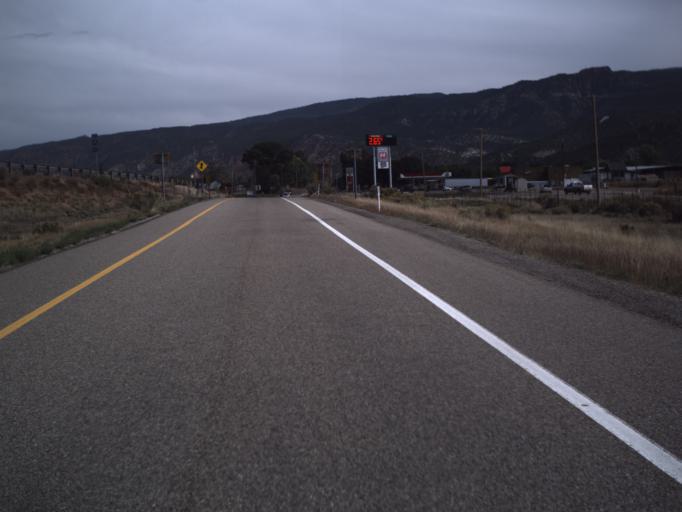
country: US
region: Utah
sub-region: Iron County
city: Parowan
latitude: 37.8383
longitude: -112.8691
